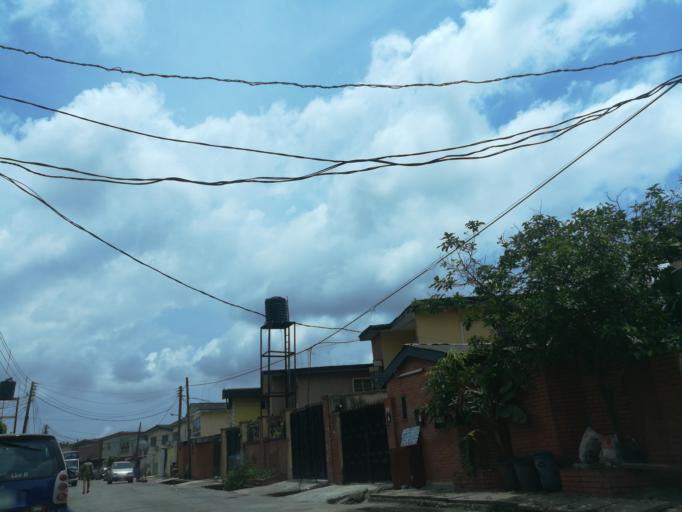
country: NG
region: Lagos
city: Somolu
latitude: 6.5496
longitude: 3.3583
